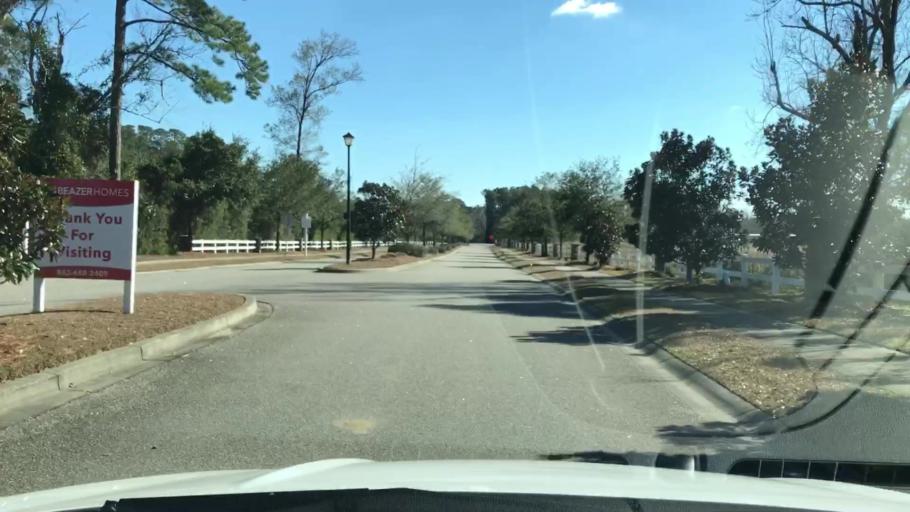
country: US
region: South Carolina
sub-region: Horry County
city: Socastee
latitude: 33.6421
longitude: -79.0337
